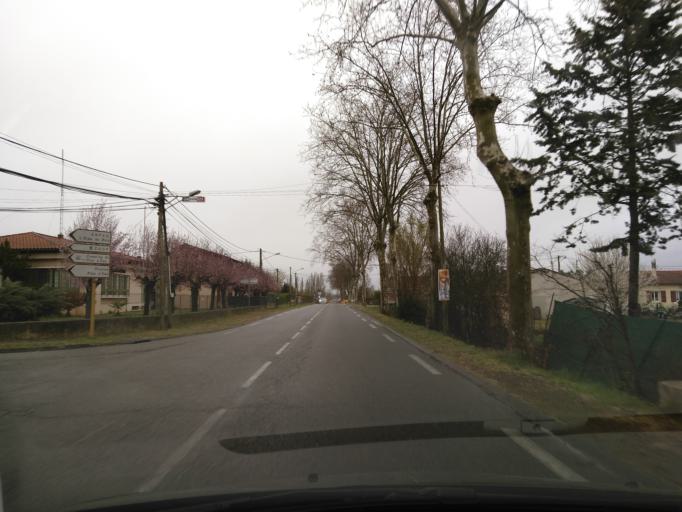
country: FR
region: Midi-Pyrenees
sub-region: Departement de la Haute-Garonne
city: Rieux-Volvestre
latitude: 43.2619
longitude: 1.1937
